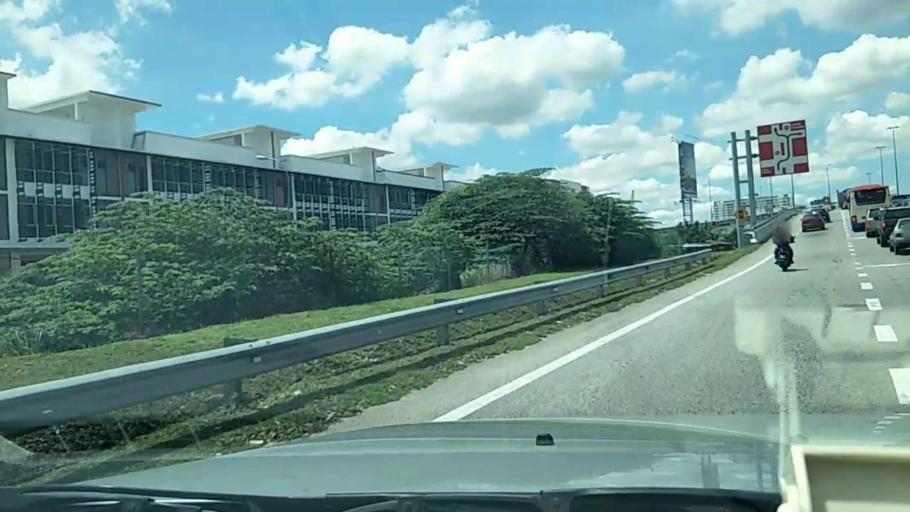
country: MY
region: Selangor
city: Subang Jaya
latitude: 2.9903
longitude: 101.6180
